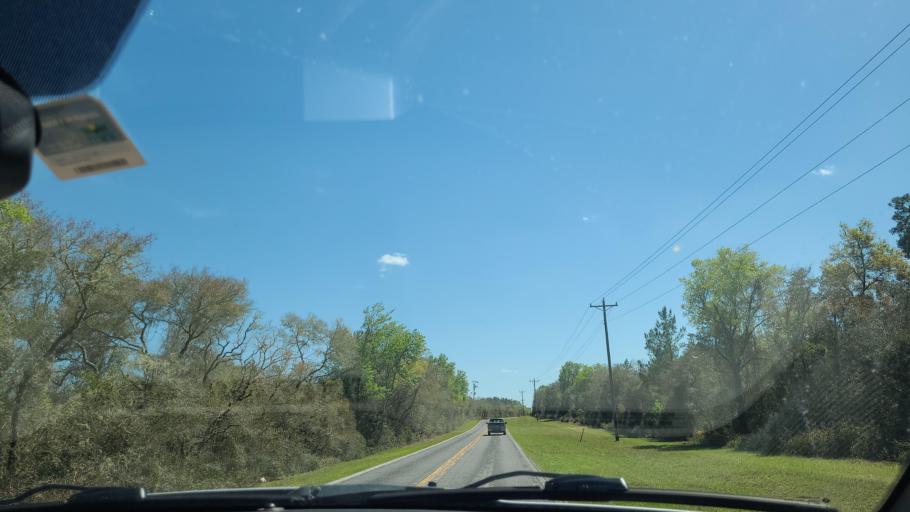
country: US
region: Florida
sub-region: Marion County
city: Citra
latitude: 29.3918
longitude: -81.8896
